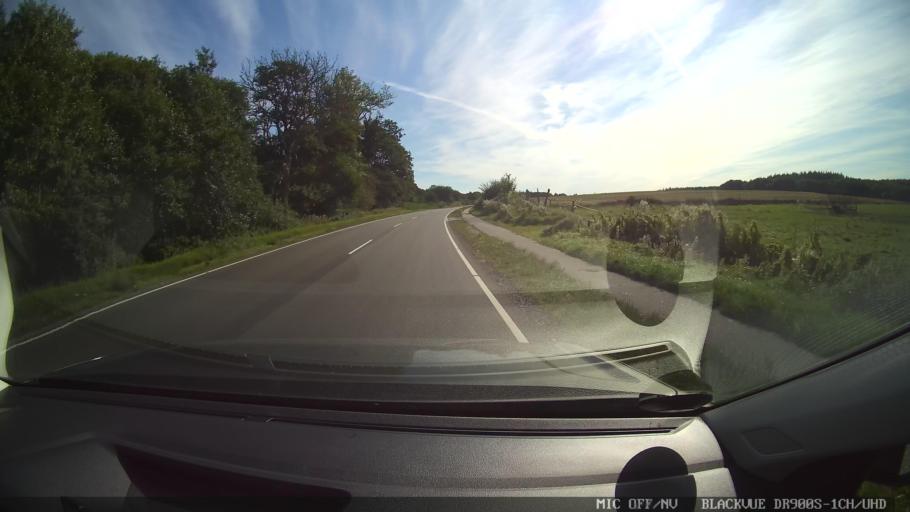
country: DK
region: North Denmark
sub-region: Mariagerfjord Kommune
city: Arden
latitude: 56.7838
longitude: 9.7299
